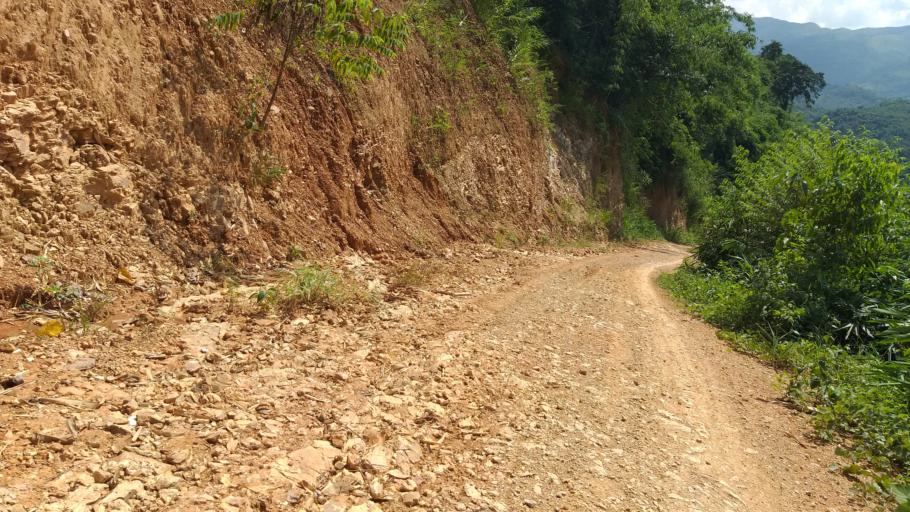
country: LA
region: Phongsali
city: Khoa
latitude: 21.3116
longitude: 102.5661
